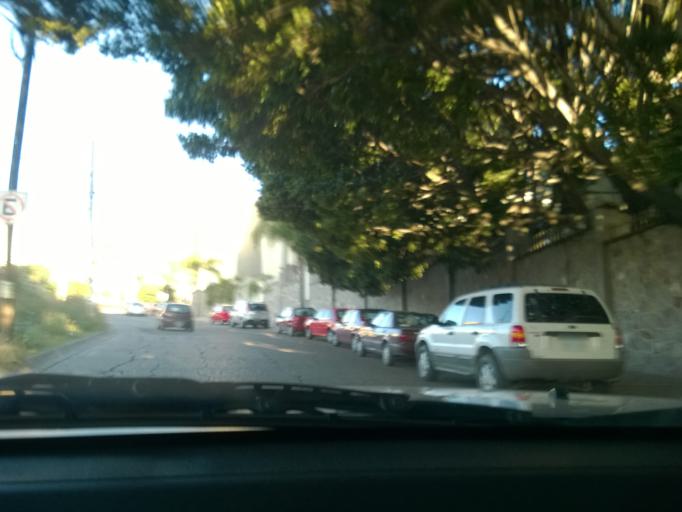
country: MX
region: Guanajuato
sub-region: Leon
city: La Ermita
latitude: 21.1511
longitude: -101.7121
